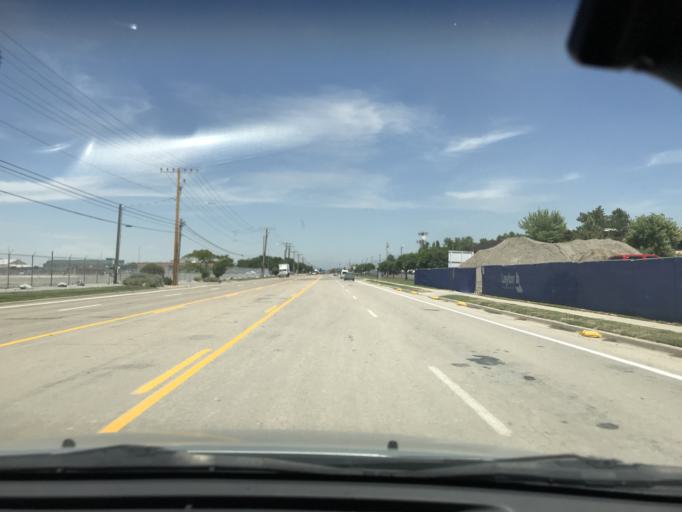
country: US
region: Utah
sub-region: Salt Lake County
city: Salt Lake City
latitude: 40.7818
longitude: -111.9535
